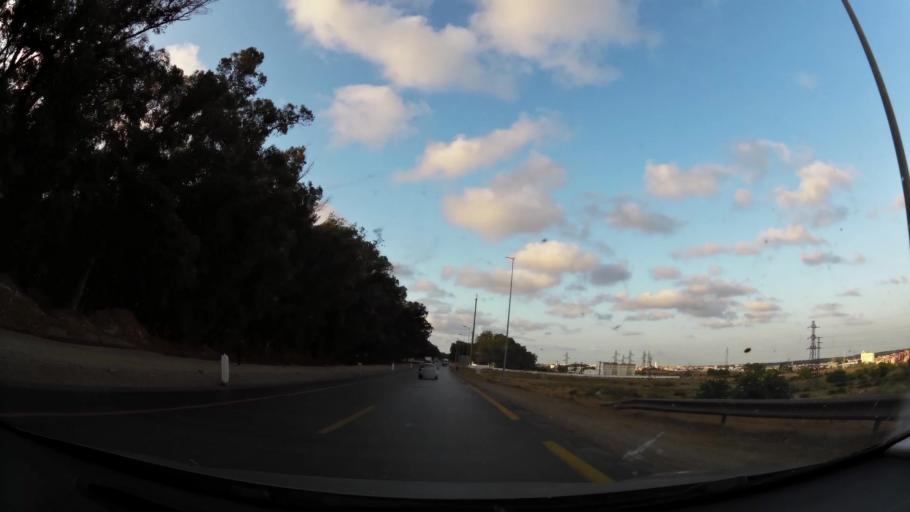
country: MA
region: Gharb-Chrarda-Beni Hssen
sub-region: Kenitra Province
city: Kenitra
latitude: 34.2368
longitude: -6.6298
